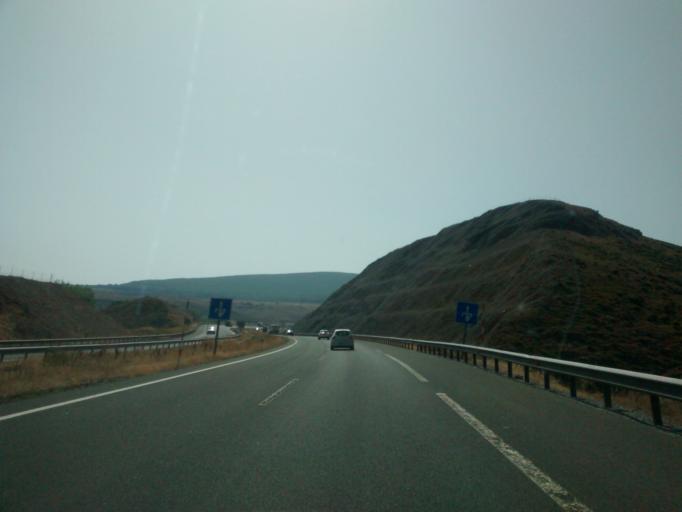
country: ES
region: Cantabria
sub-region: Provincia de Cantabria
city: Villaescusa
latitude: 42.9482
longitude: -4.1369
